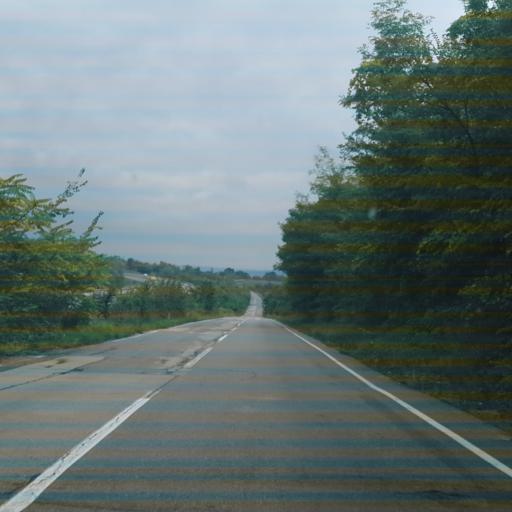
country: RS
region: Central Serbia
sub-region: Nisavski Okrug
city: Razanj
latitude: 43.6272
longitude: 21.5663
